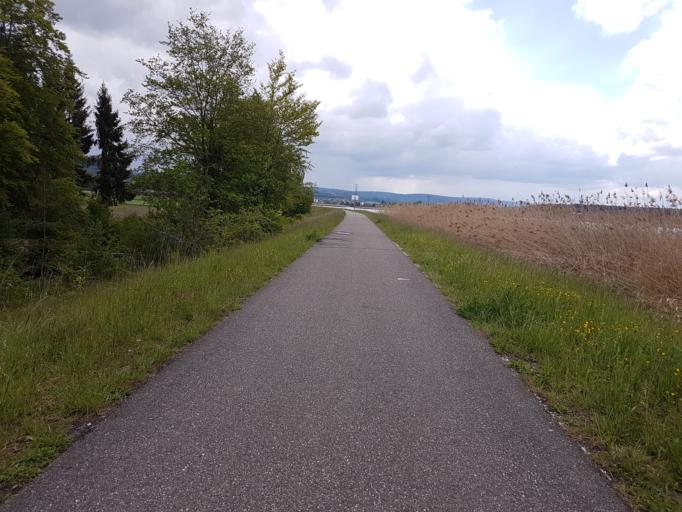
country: CH
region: Aargau
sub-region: Bezirk Zurzach
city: Koblenz
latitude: 47.5903
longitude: 8.2317
